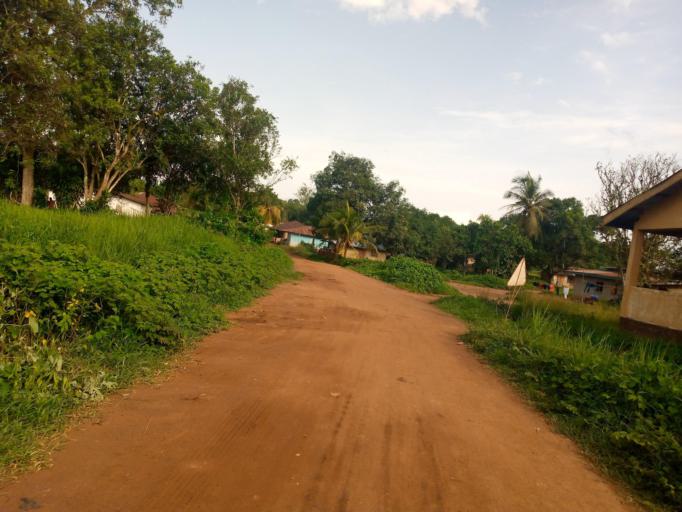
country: SL
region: Southern Province
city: Sumbuya
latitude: 7.6140
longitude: -12.1438
